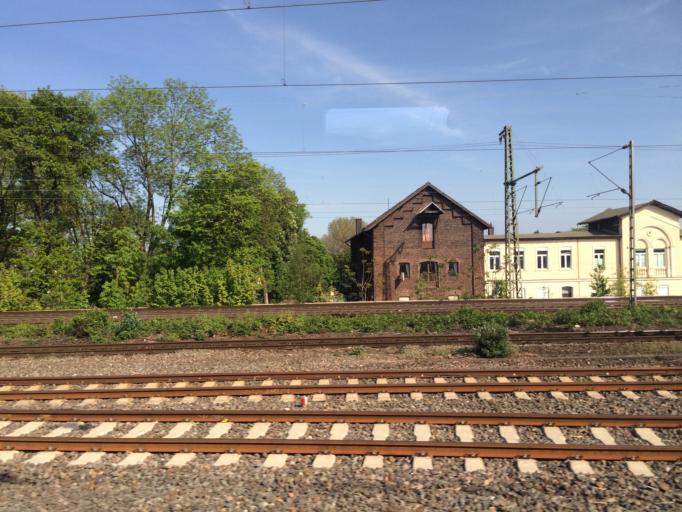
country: DE
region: North Rhine-Westphalia
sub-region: Regierungsbezirk Koln
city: Buchheim
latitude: 50.9633
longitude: 7.0176
